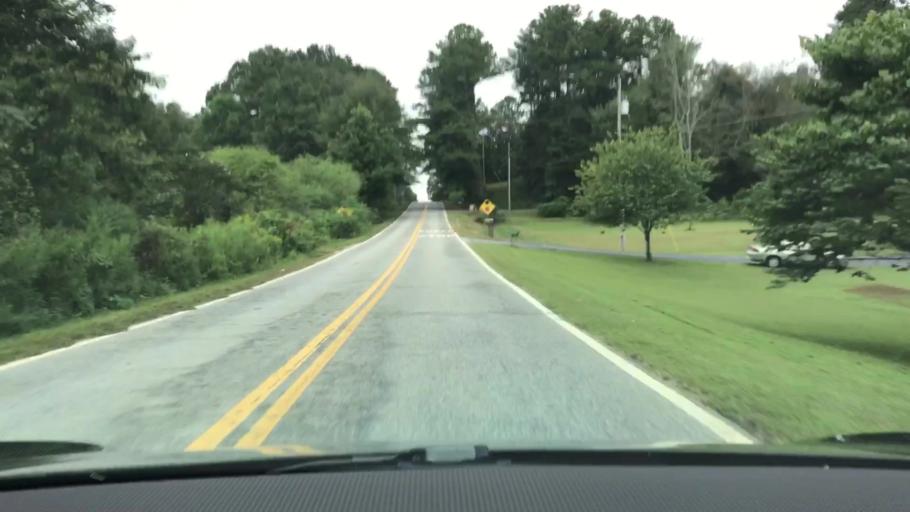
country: US
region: Georgia
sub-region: Barrow County
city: Auburn
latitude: 34.0496
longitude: -83.8156
